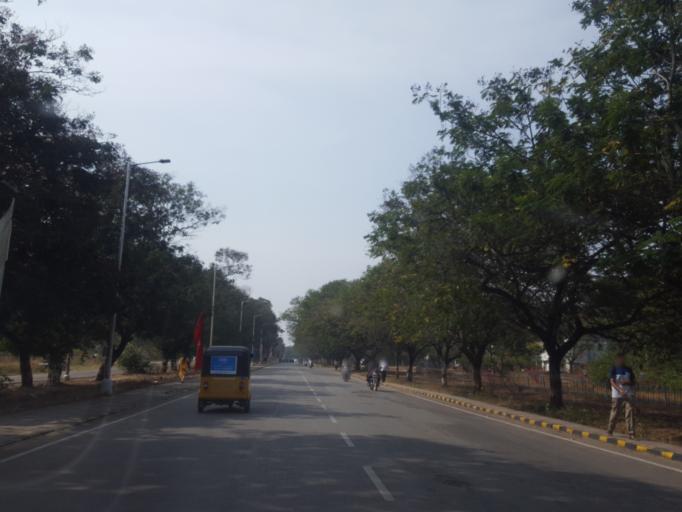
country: IN
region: Telangana
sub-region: Medak
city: Serilingampalle
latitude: 17.4941
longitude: 78.3138
